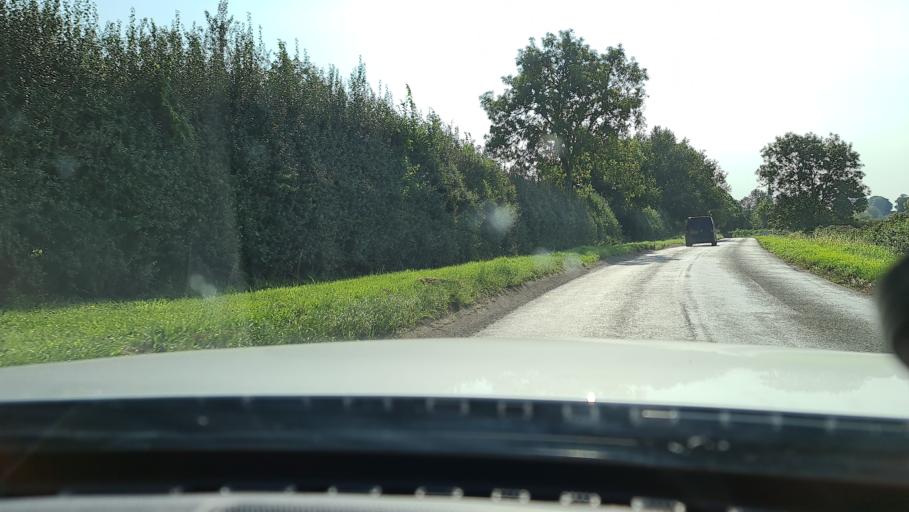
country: GB
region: England
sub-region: Oxfordshire
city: Adderbury
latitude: 52.0291
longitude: -1.2816
